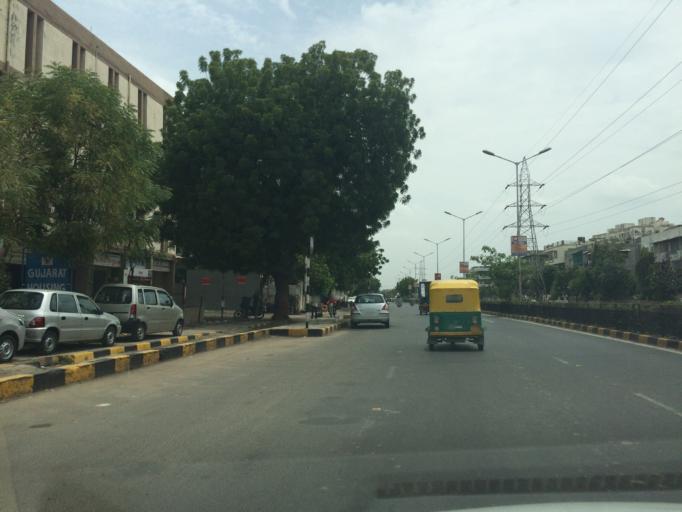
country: IN
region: Gujarat
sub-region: Ahmadabad
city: Ahmedabad
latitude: 23.0640
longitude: 72.5553
